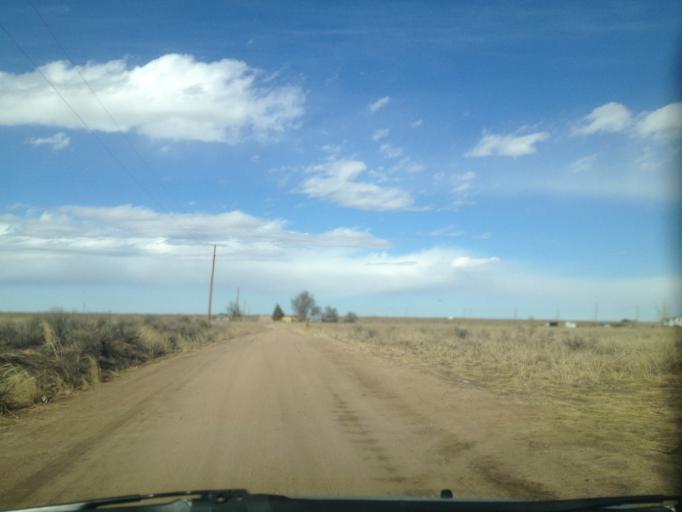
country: US
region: Colorado
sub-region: Weld County
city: Keenesburg
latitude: 40.2875
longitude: -104.2591
